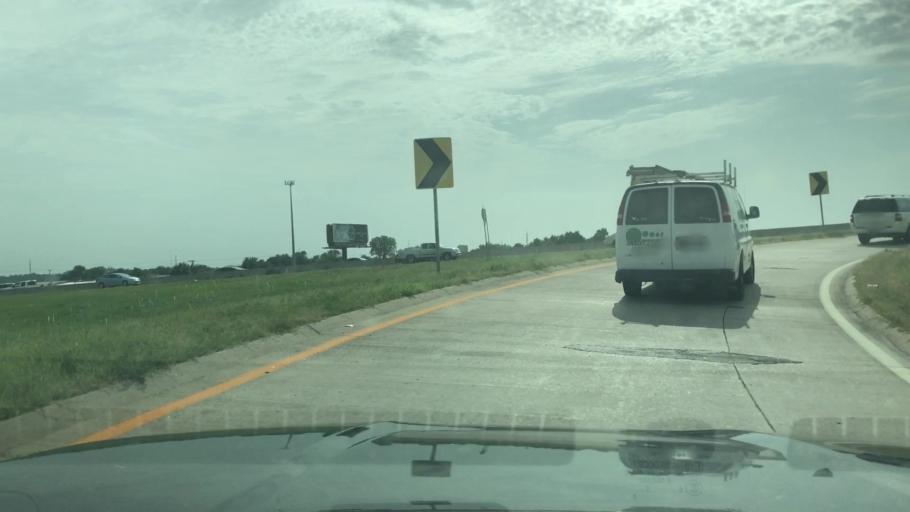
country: US
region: Oklahoma
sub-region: Tulsa County
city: Broken Arrow
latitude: 36.0969
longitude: -95.8589
